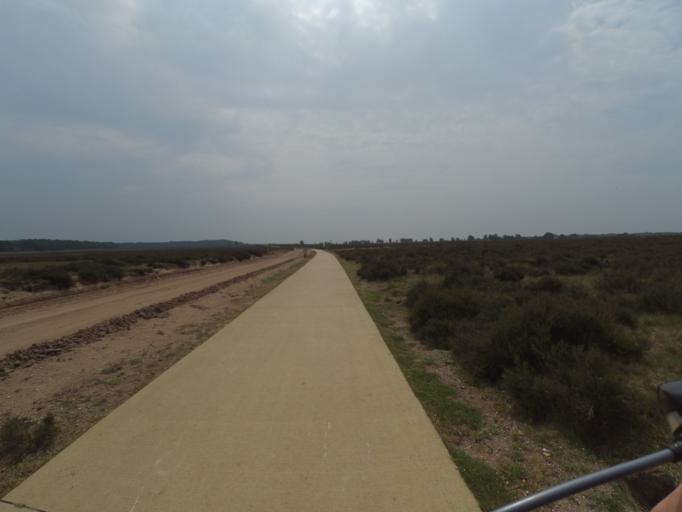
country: NL
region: Gelderland
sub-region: Gemeente Ede
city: Ede
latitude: 52.0461
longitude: 5.7117
